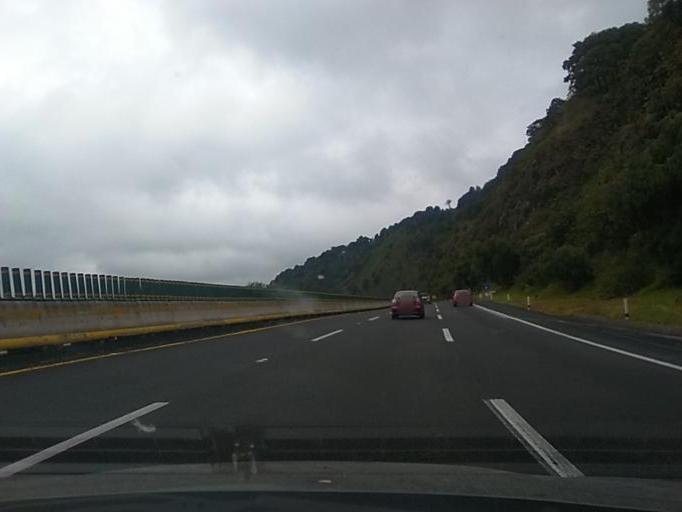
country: MX
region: Mexico City
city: Xochimilco
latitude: 19.2174
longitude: -99.1310
